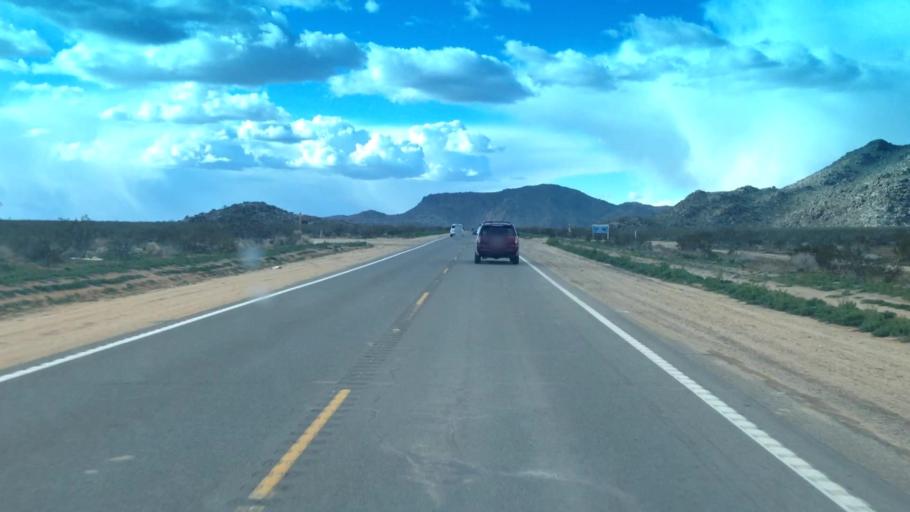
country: US
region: California
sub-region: San Bernardino County
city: Lucerne Valley
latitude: 34.4588
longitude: -117.0761
